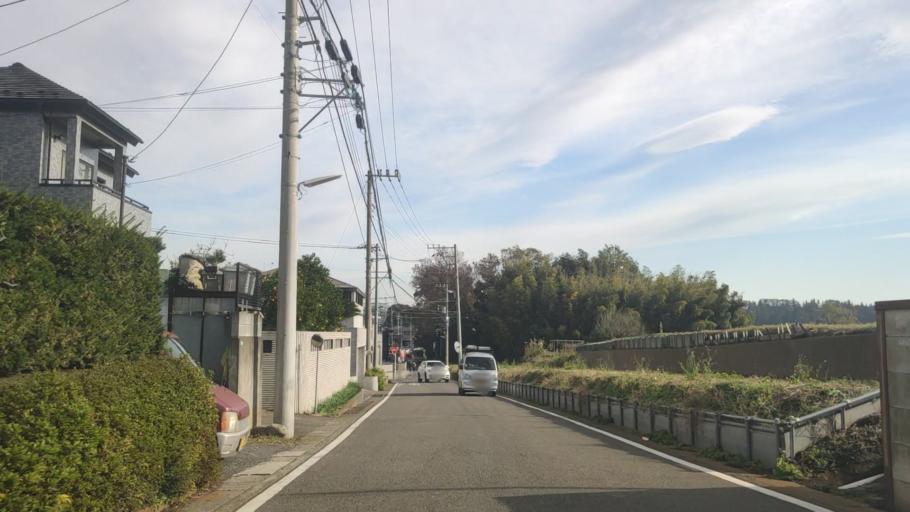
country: JP
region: Kanagawa
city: Atsugi
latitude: 35.4312
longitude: 139.3942
